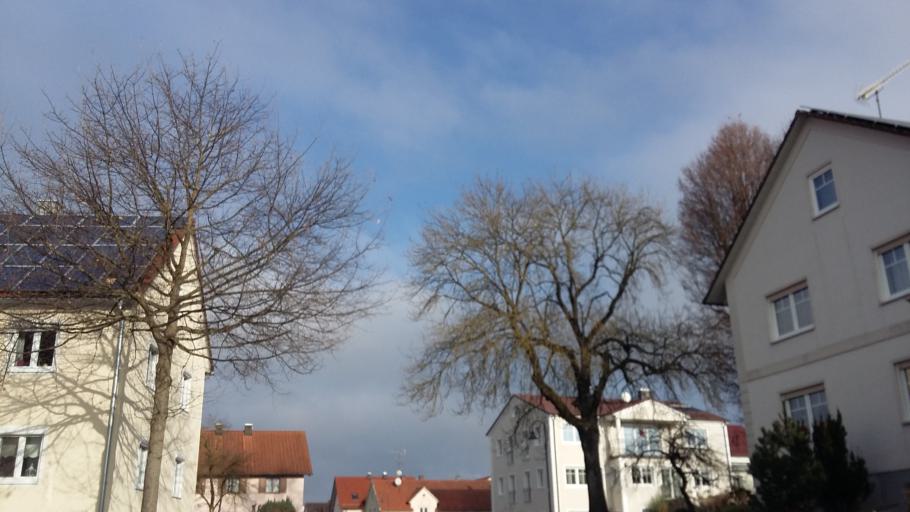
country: DE
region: Bavaria
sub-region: Swabia
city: Sielenbach
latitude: 48.3972
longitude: 11.1647
